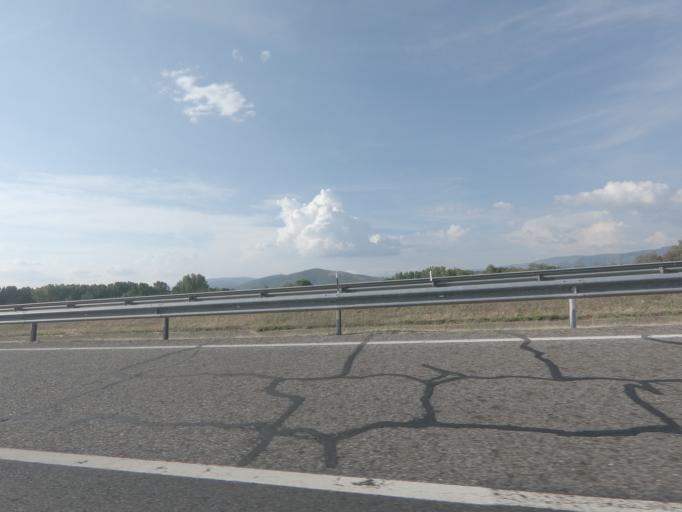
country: ES
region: Galicia
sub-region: Provincia de Ourense
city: Verin
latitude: 41.9219
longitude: -7.4626
